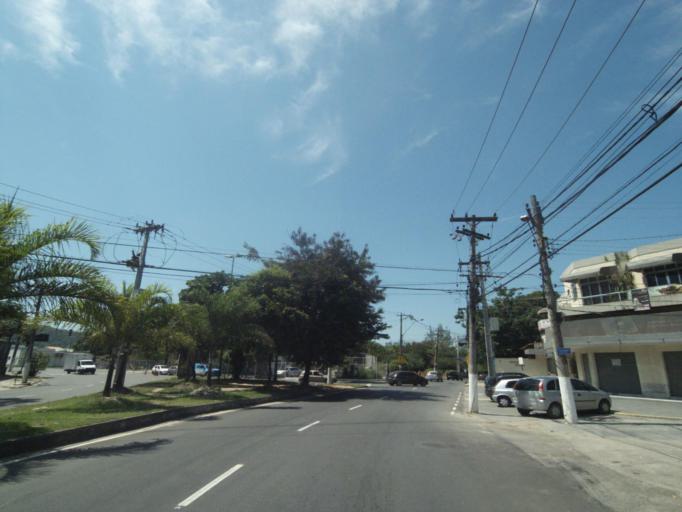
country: BR
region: Rio de Janeiro
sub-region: Sao Goncalo
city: Sao Goncalo
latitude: -22.8790
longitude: -43.0269
